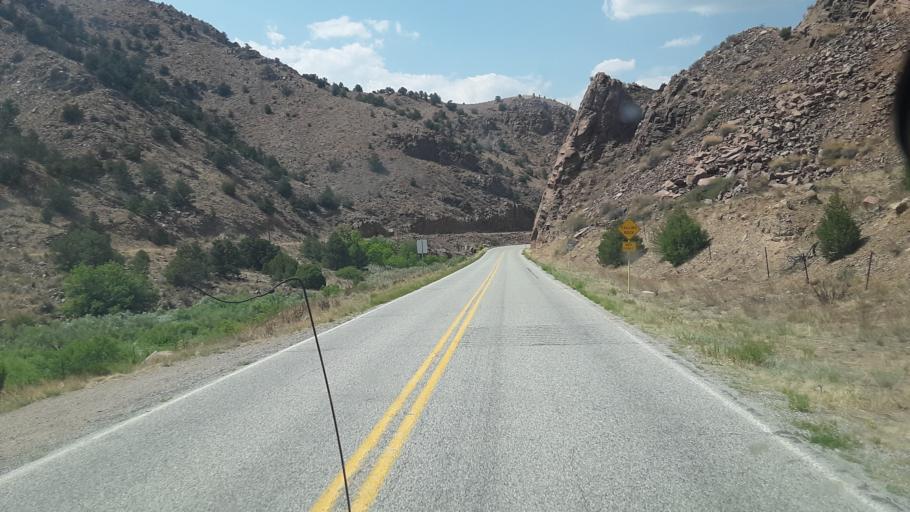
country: US
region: Colorado
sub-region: Custer County
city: Westcliffe
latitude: 38.4031
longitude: -105.5837
